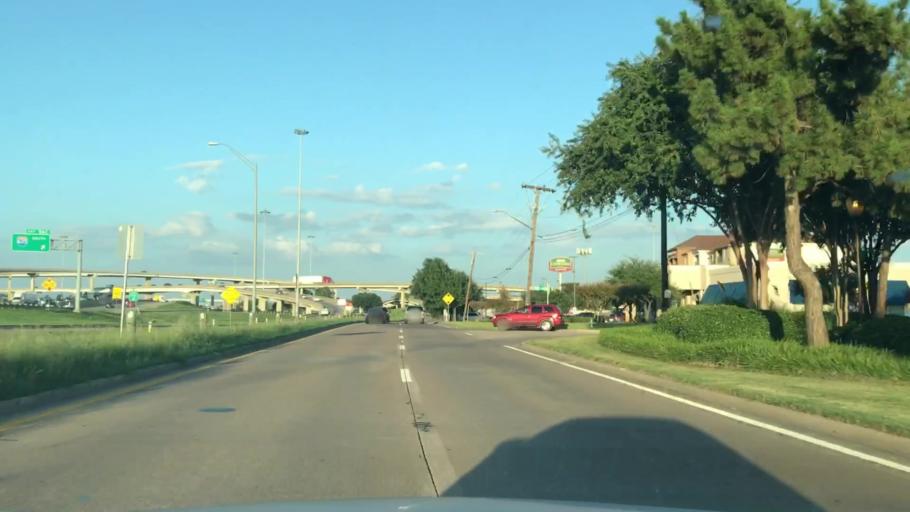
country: US
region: Texas
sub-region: Dallas County
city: Mesquite
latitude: 32.8201
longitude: -96.6342
